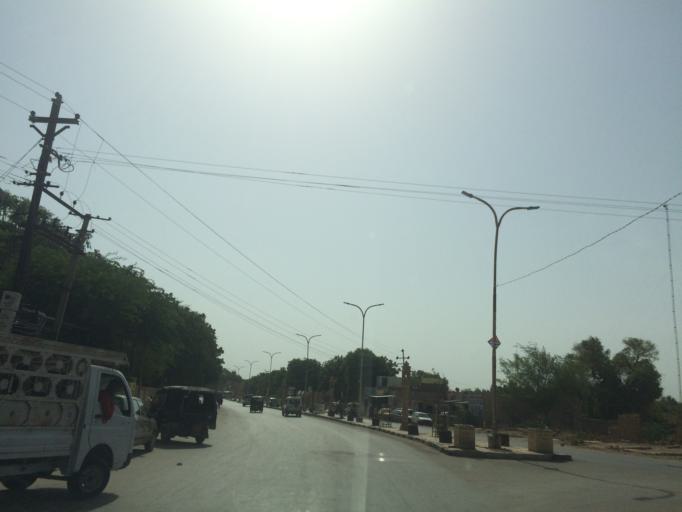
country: IN
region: Rajasthan
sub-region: Jaisalmer
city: Jaisalmer
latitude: 26.9091
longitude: 70.9125
